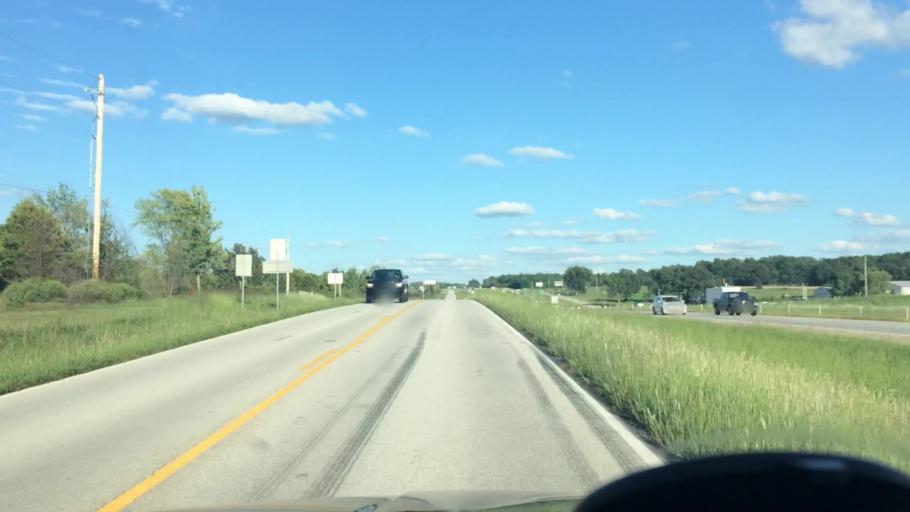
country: US
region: Missouri
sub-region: Greene County
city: Strafford
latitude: 37.2697
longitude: -93.0816
